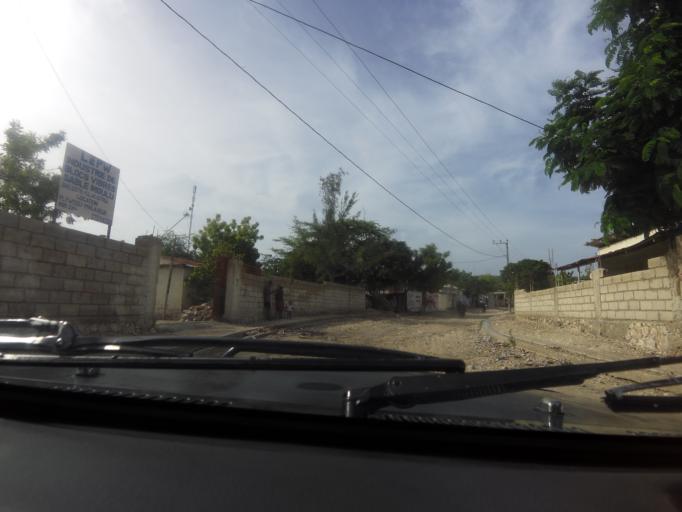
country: HT
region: Ouest
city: Anse a Galets
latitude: 18.8354
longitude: -72.8631
